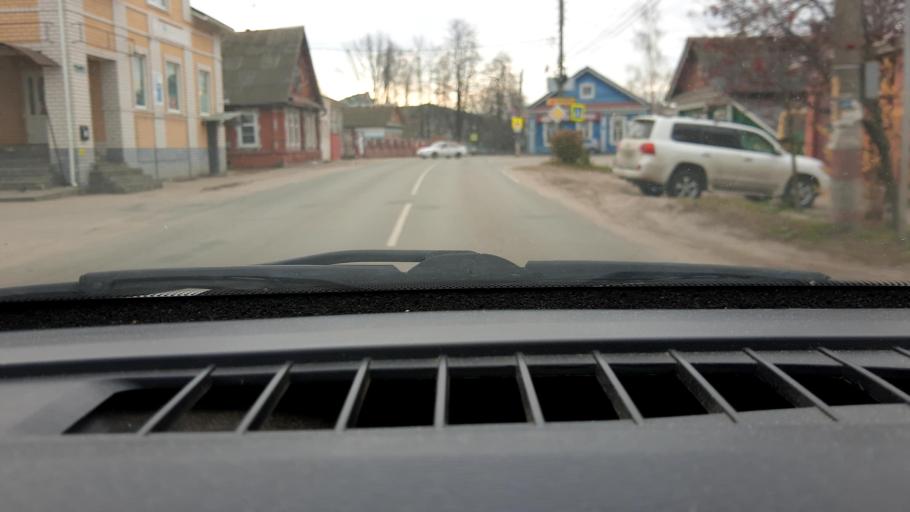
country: RU
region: Nizjnij Novgorod
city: Gorodets
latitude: 56.6434
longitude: 43.4747
